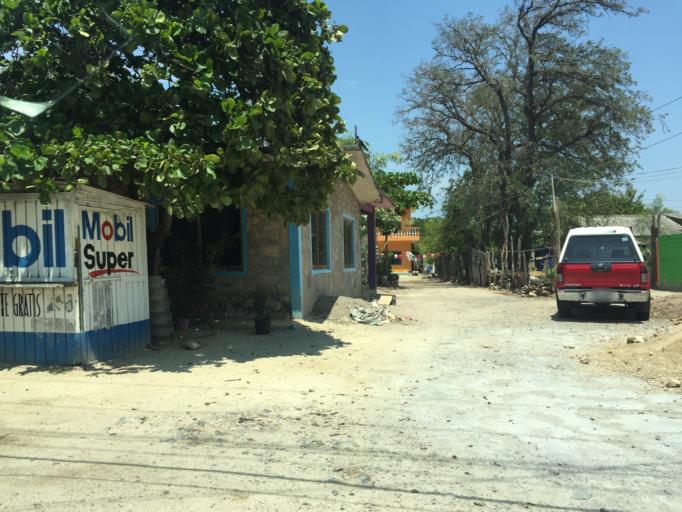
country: MX
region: Oaxaca
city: Asuncion Ixtaltepec
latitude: 16.5051
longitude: -95.0639
